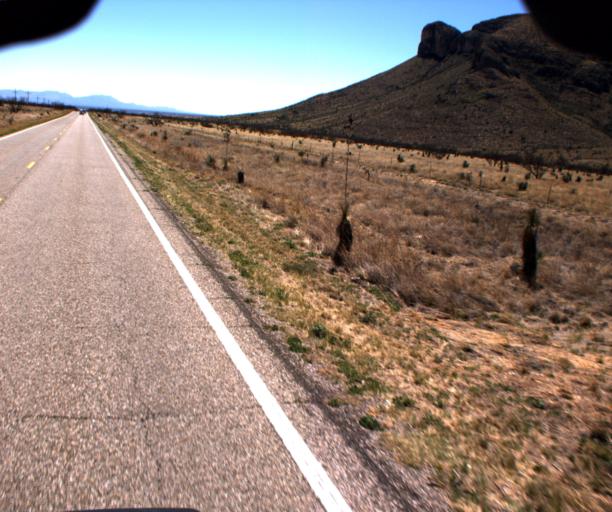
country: US
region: Arizona
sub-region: Cochise County
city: Huachuca City
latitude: 31.7040
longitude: -110.4362
